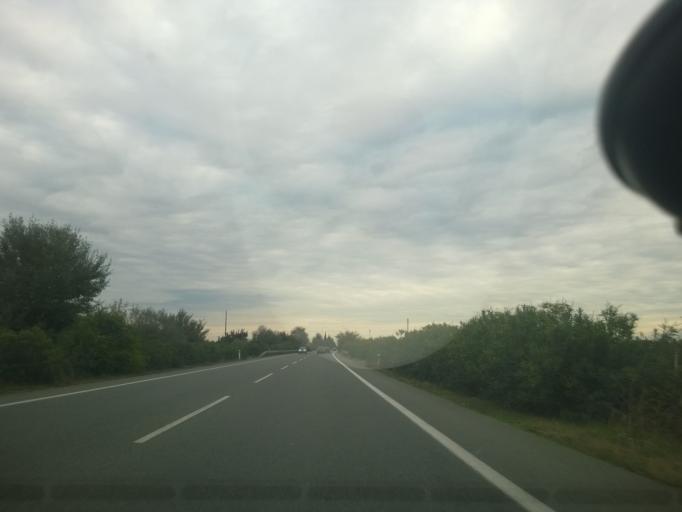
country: GR
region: Central Macedonia
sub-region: Nomos Pellis
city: Palaifyto
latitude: 40.8038
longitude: 22.2544
